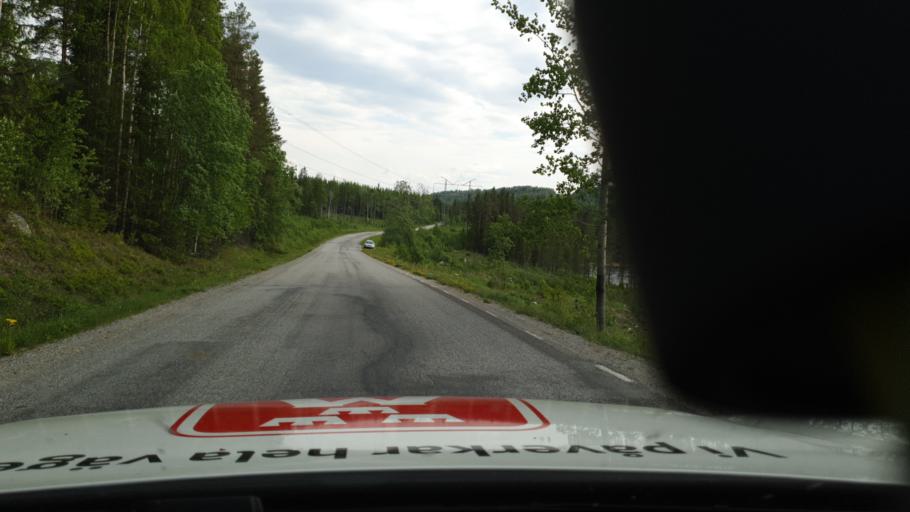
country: SE
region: Jaemtland
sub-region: Braecke Kommun
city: Braecke
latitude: 63.0049
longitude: 15.1977
